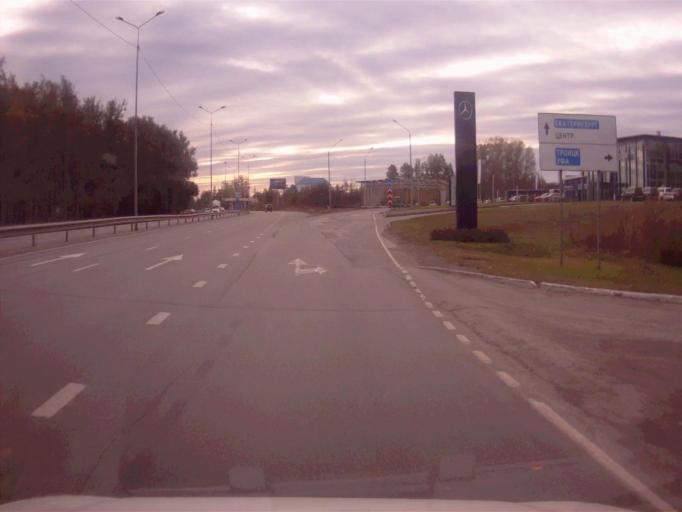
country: RU
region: Chelyabinsk
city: Novosineglazovskiy
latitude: 55.0827
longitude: 61.3932
